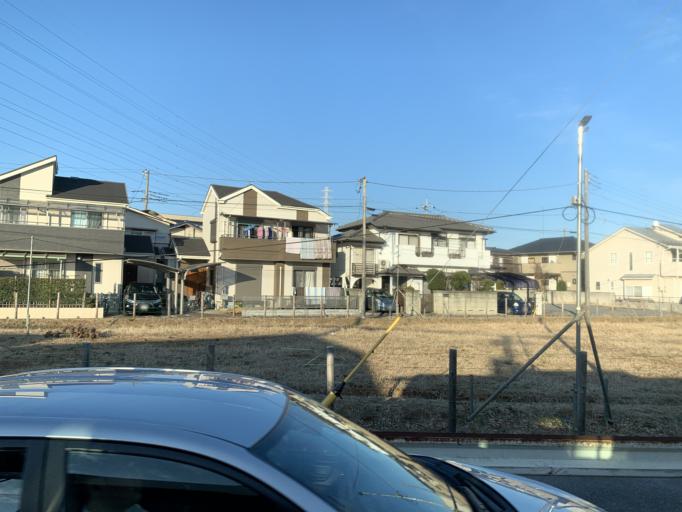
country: JP
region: Chiba
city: Kashiwa
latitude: 35.8679
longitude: 139.9566
